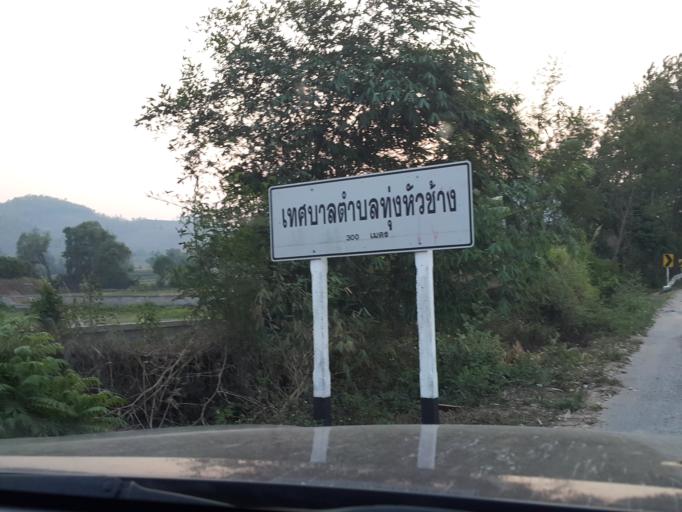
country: TH
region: Lamphun
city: Thung Hua Chang
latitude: 17.9816
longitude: 99.0359
